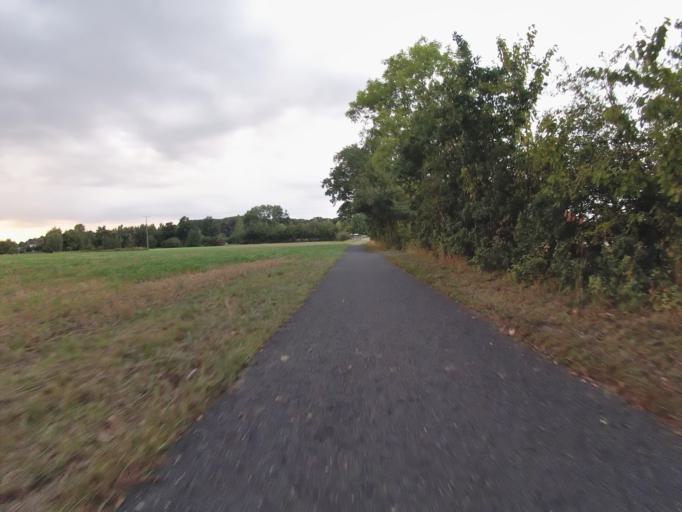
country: DE
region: North Rhine-Westphalia
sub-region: Regierungsbezirk Munster
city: Westerkappeln
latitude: 52.2777
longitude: 7.8638
